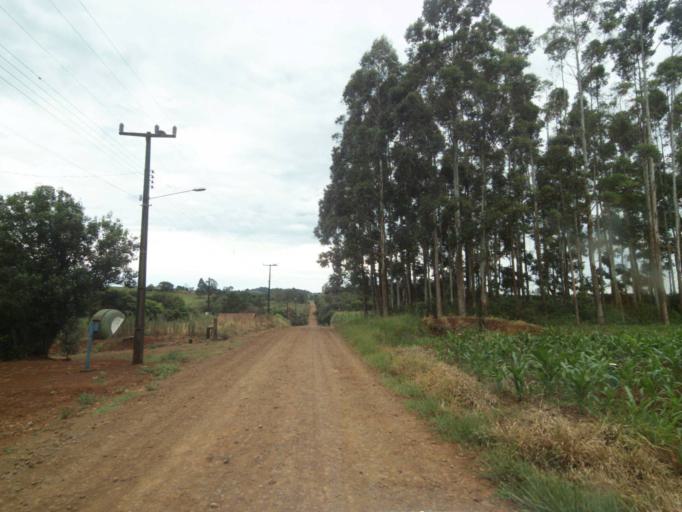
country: BR
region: Parana
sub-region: Guaraniacu
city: Guaraniacu
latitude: -24.9142
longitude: -52.9363
